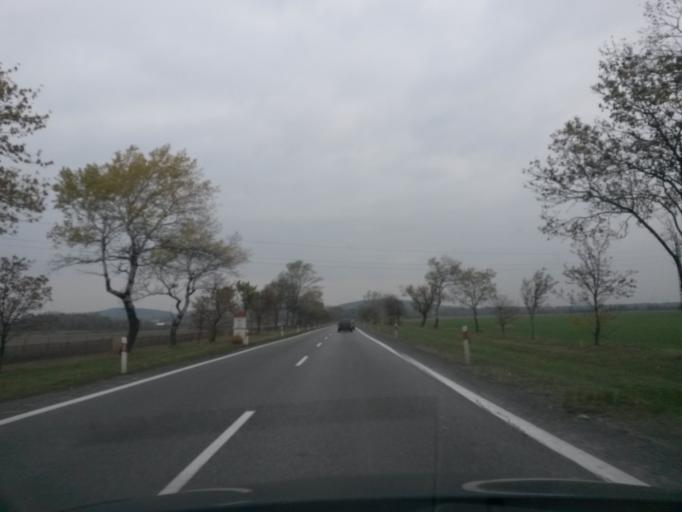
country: PL
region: Lower Silesian Voivodeship
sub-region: Powiat zabkowicki
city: Bardo
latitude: 50.5149
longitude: 16.7605
